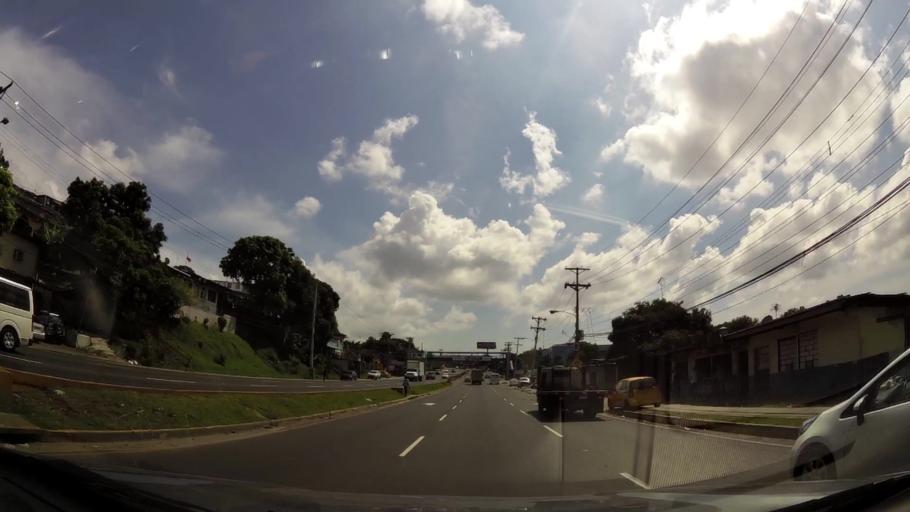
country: PA
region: Panama
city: San Miguelito
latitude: 9.0297
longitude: -79.4979
